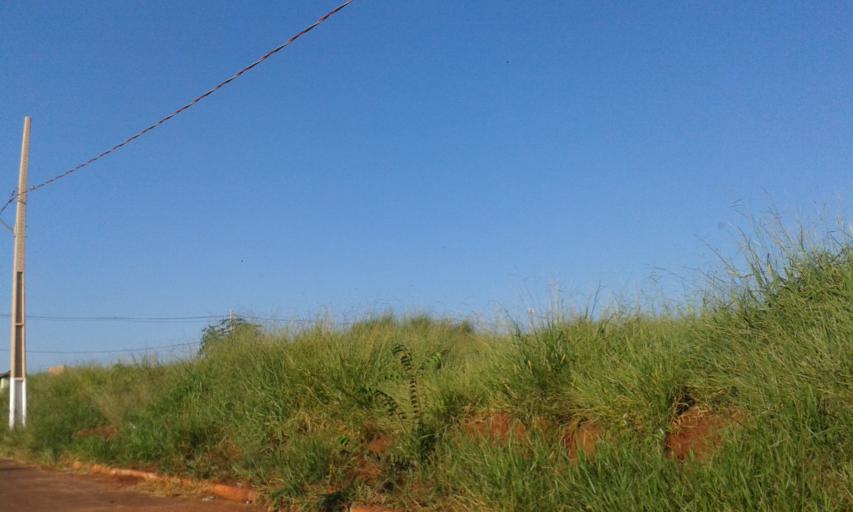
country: BR
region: Minas Gerais
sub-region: Ituiutaba
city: Ituiutaba
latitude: -19.0139
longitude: -49.4516
